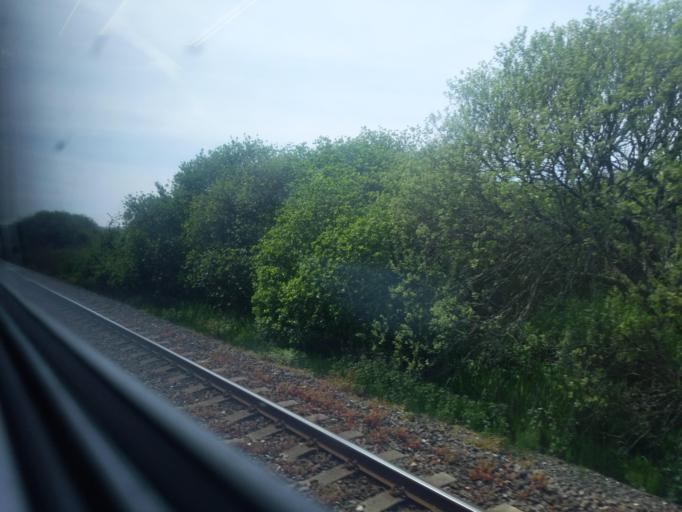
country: GB
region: England
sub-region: Cornwall
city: Marazion
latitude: 50.1332
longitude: -5.4808
